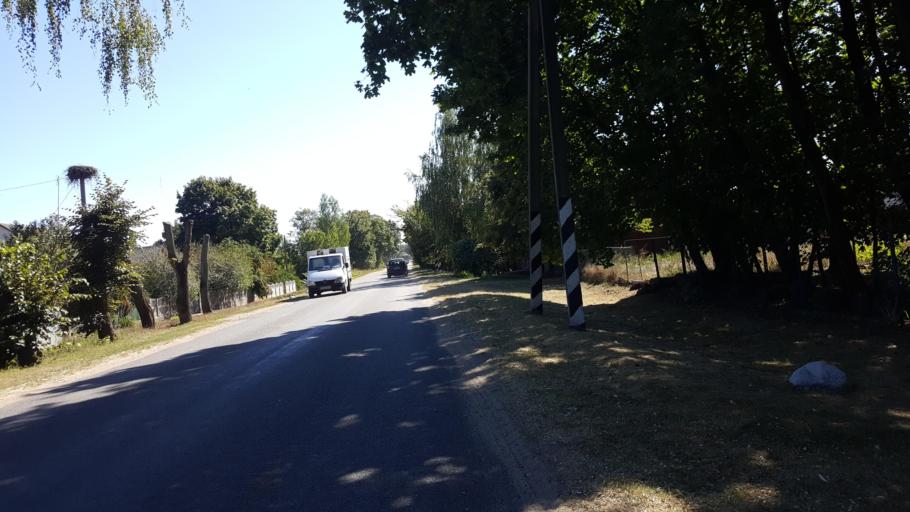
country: PL
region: Lublin Voivodeship
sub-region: Powiat bialski
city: Rokitno
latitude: 52.2329
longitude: 23.3422
